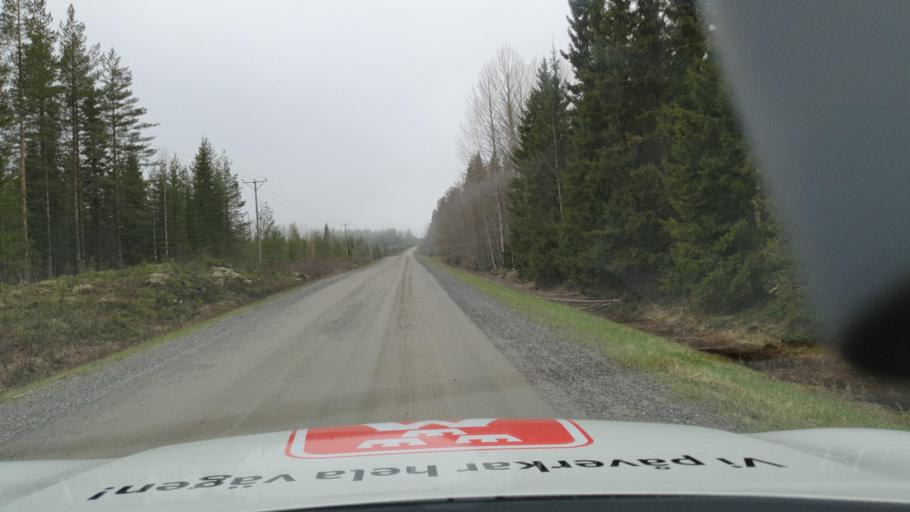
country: SE
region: Vaesterbotten
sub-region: Nordmalings Kommun
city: Nordmaling
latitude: 63.7658
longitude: 19.4724
